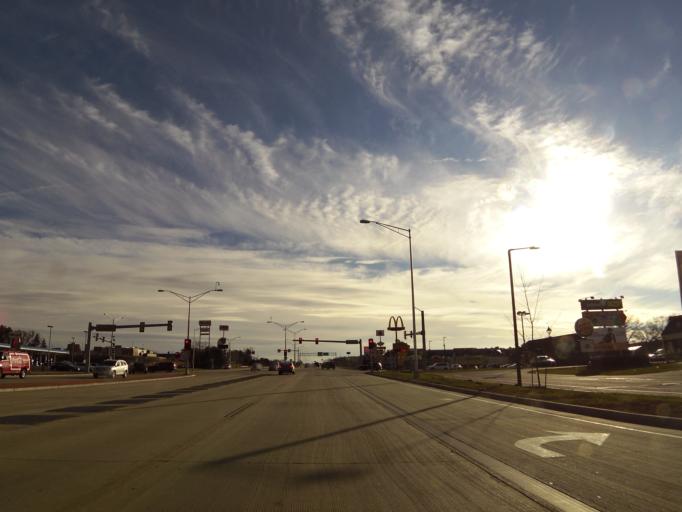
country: US
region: Wisconsin
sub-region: Sauk County
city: Lake Delton
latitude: 43.5764
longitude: -89.7786
